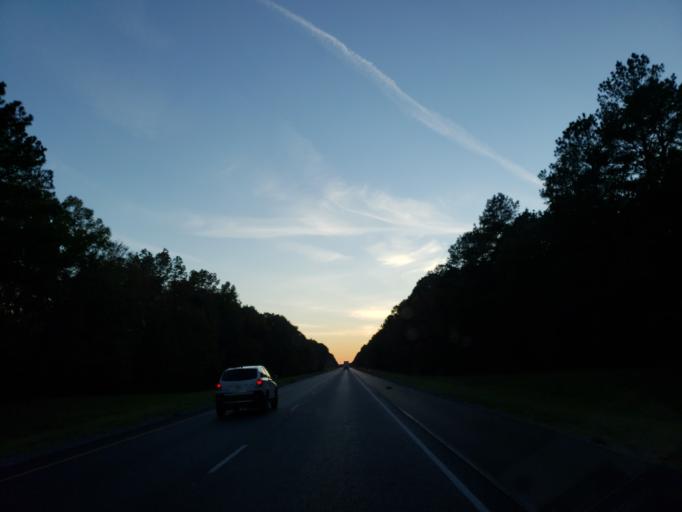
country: US
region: Alabama
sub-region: Sumter County
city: Livingston
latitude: 32.5779
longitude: -88.2392
